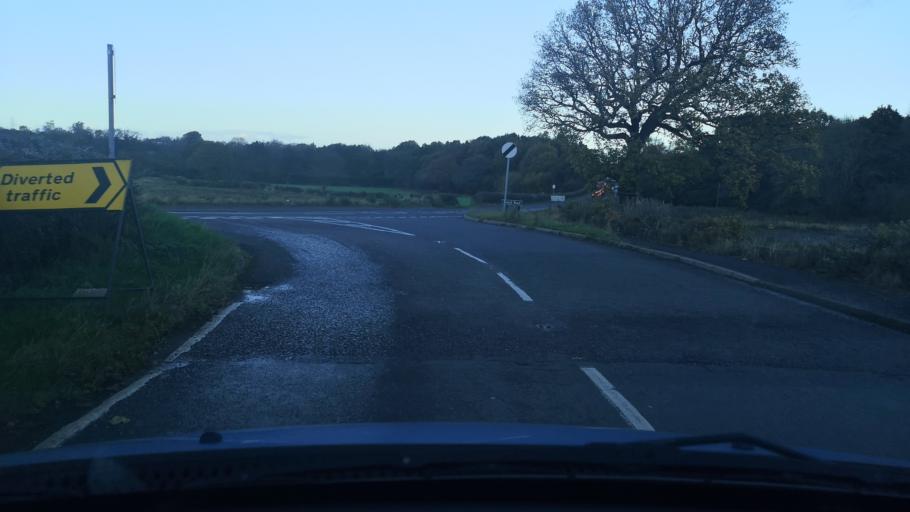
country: GB
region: England
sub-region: City and Borough of Wakefield
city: Crigglestone
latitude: 53.6386
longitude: -1.5481
